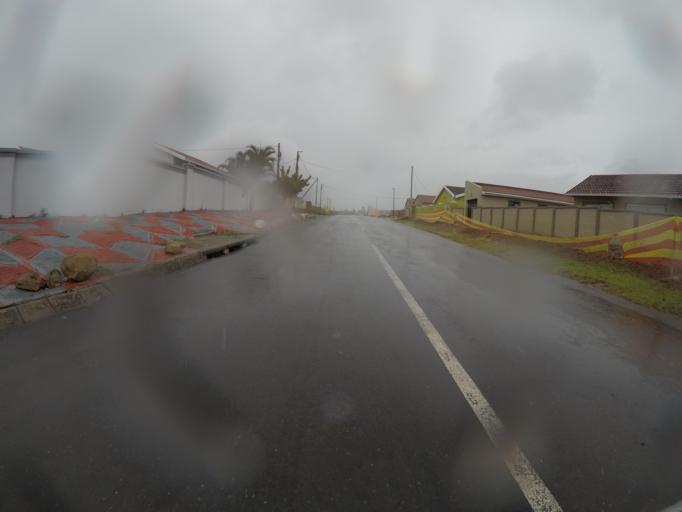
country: ZA
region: Eastern Cape
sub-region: Buffalo City Metropolitan Municipality
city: East London
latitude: -32.9961
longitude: 27.8414
